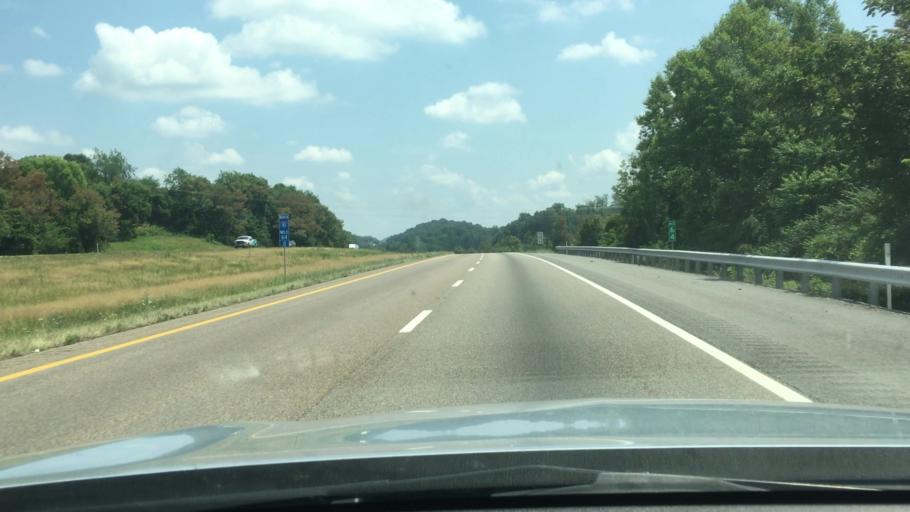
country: US
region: Tennessee
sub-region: Washington County
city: Spurgeon
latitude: 36.5112
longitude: -82.4181
